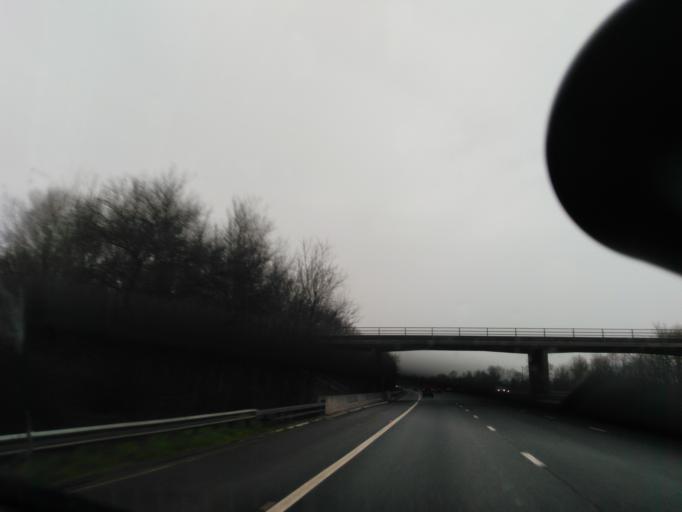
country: GB
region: England
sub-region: Gloucestershire
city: Stonehouse
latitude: 51.7789
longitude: -2.3078
